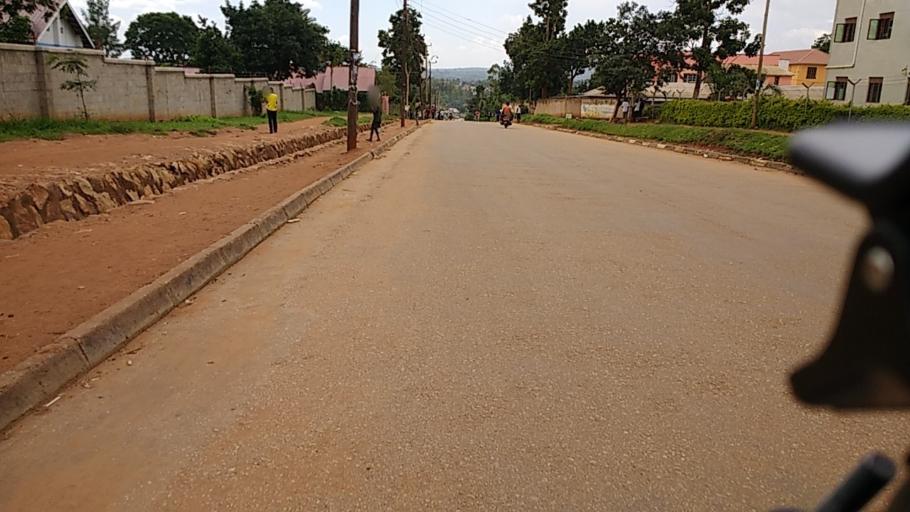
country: UG
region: Eastern Region
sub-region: Mbale District
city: Mbale
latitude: 1.0808
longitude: 34.1711
